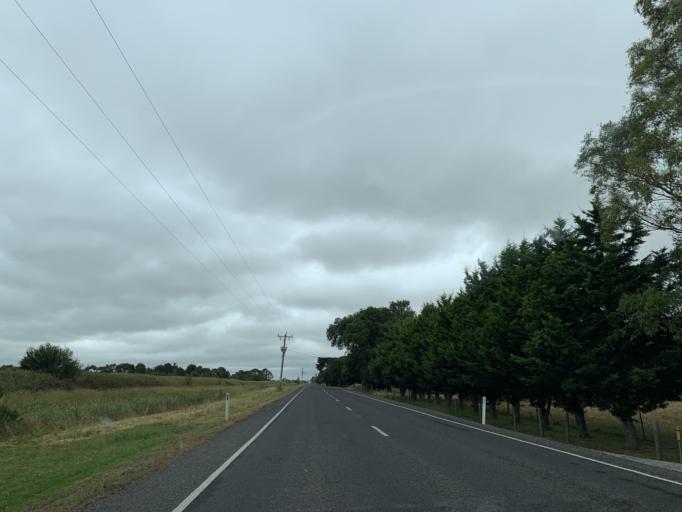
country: AU
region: Victoria
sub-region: Cardinia
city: Pakenham South
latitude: -38.1834
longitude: 145.6043
